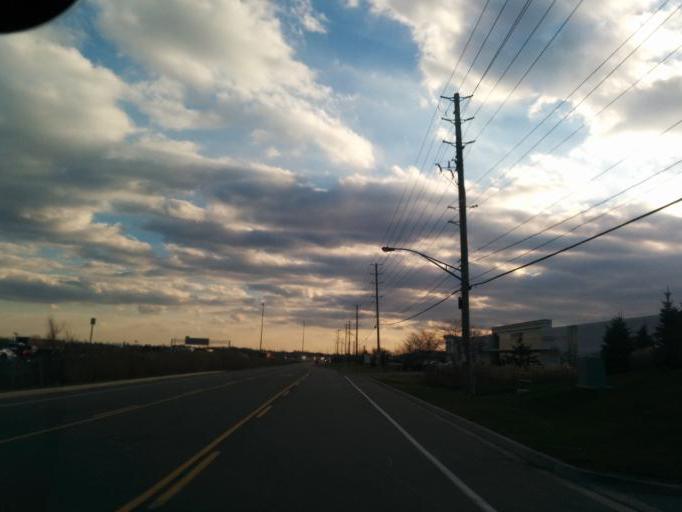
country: CA
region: Ontario
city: Oakville
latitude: 43.4799
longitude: -79.6731
